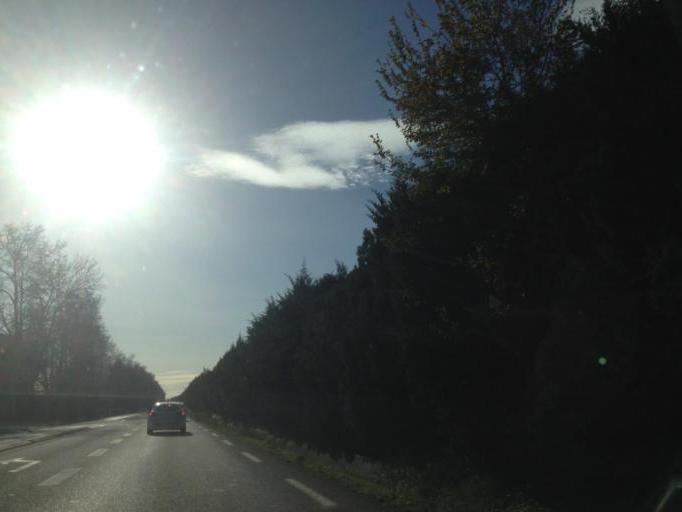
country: FR
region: Provence-Alpes-Cote d'Azur
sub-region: Departement du Vaucluse
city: Courthezon
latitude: 44.0787
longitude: 4.8810
